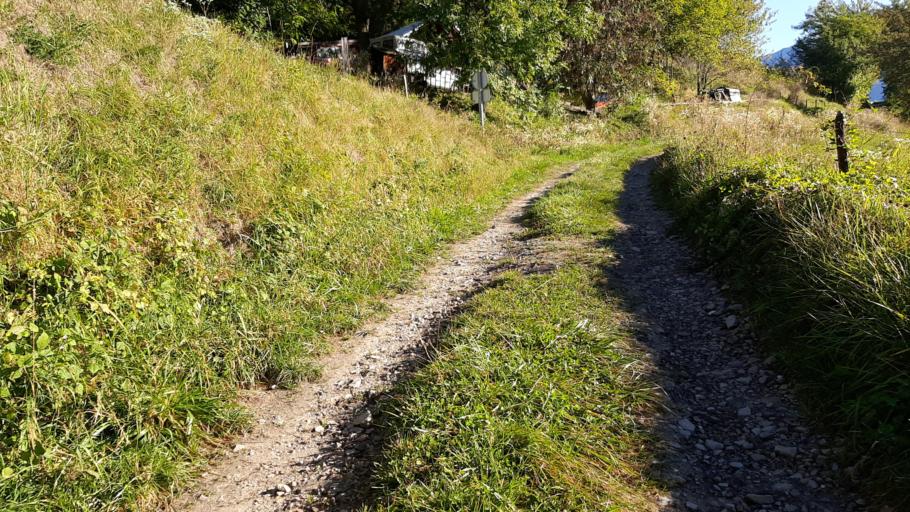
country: FR
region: Rhone-Alpes
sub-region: Departement de la Savoie
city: Saint-Jean-de-Maurienne
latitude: 45.2754
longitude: 6.3139
